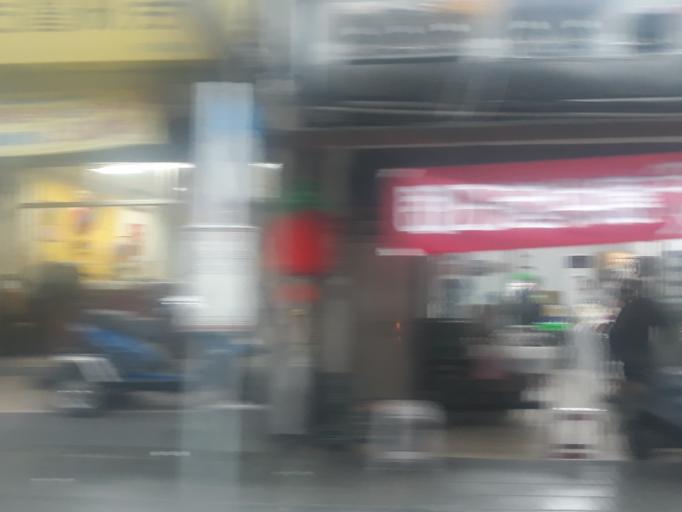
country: TW
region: Taipei
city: Taipei
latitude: 24.9877
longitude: 121.5699
